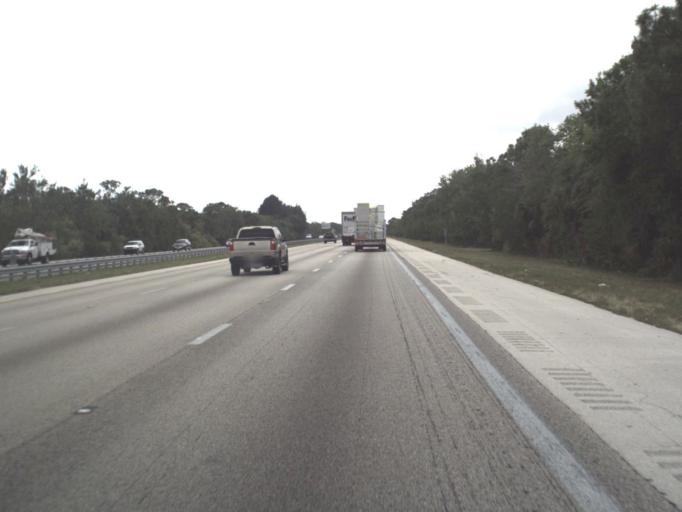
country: US
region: Florida
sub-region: Brevard County
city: South Patrick Shores
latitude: 28.1754
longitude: -80.7060
